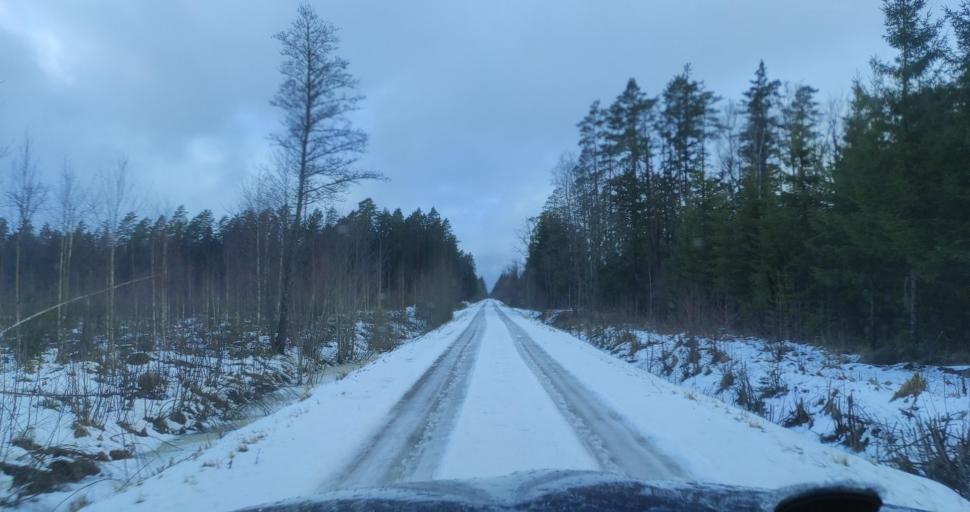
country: LV
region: Dundaga
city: Dundaga
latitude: 57.4065
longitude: 22.0926
